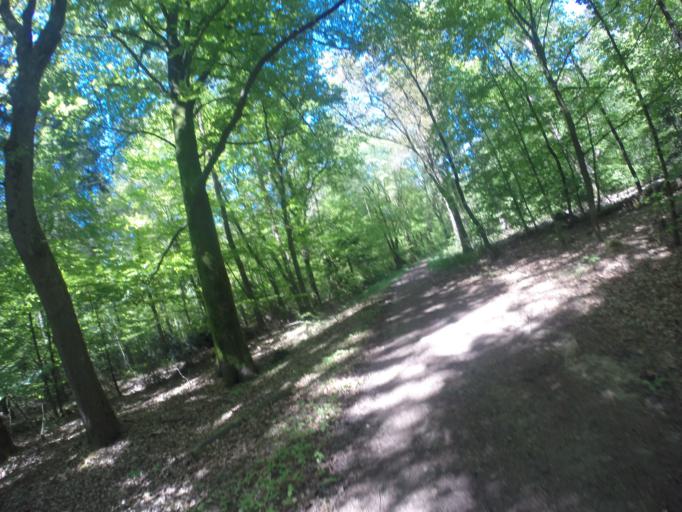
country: NL
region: Gelderland
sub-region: Gemeente Montferland
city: s-Heerenberg
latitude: 51.9112
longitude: 6.2344
